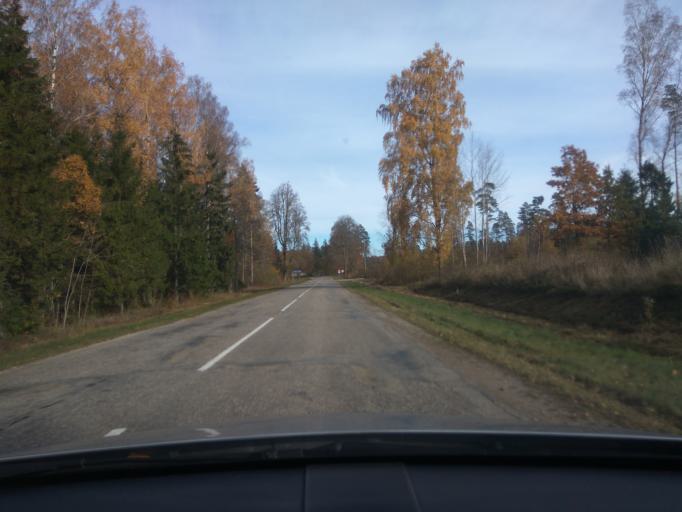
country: LV
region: Alsunga
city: Alsunga
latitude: 56.9933
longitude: 21.6221
